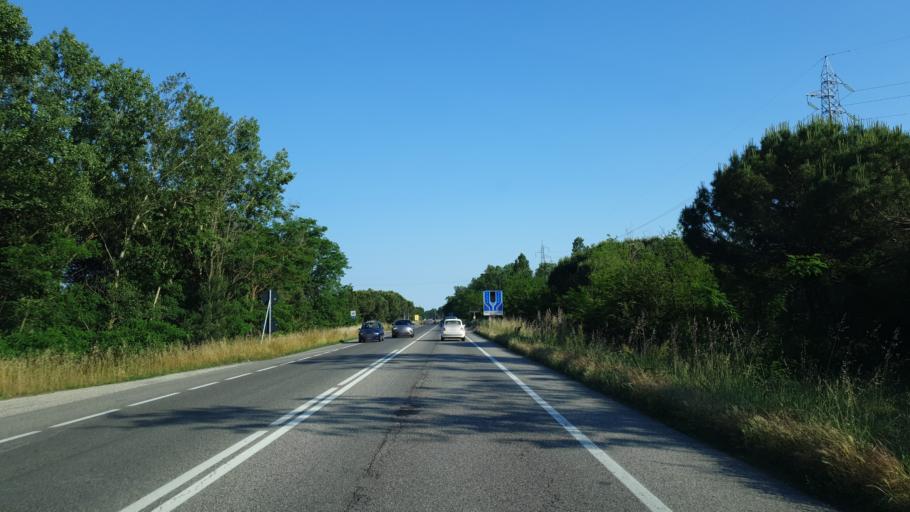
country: IT
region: Emilia-Romagna
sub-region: Provincia di Ravenna
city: Fosso Ghiaia
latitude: 44.3412
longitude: 12.2662
